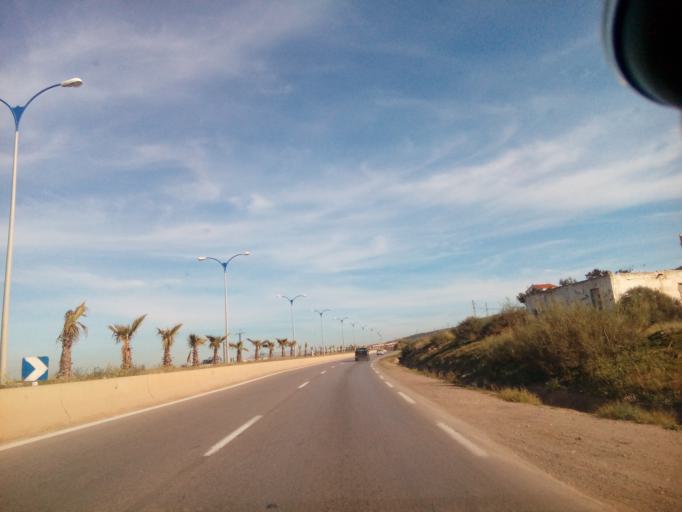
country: DZ
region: Mostaganem
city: Mostaganem
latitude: 35.8722
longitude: 0.0403
